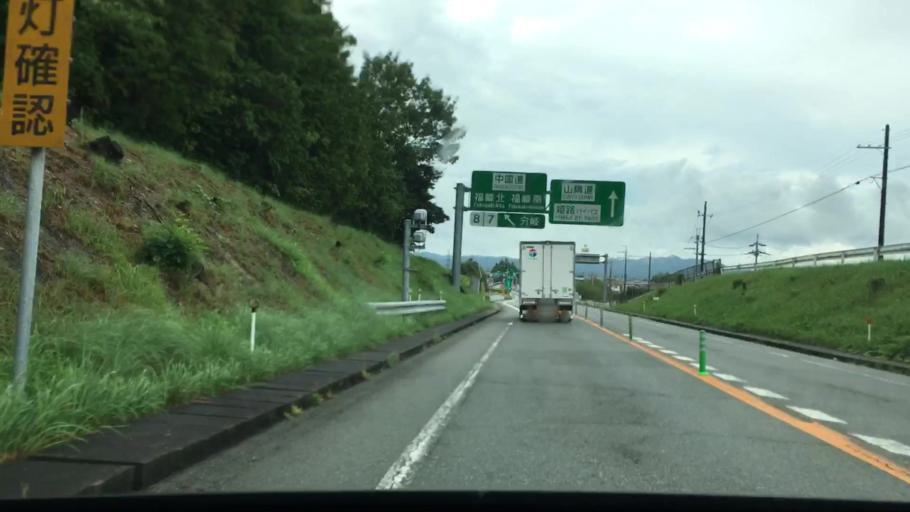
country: JP
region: Hyogo
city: Himeji
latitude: 34.9602
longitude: 134.7698
